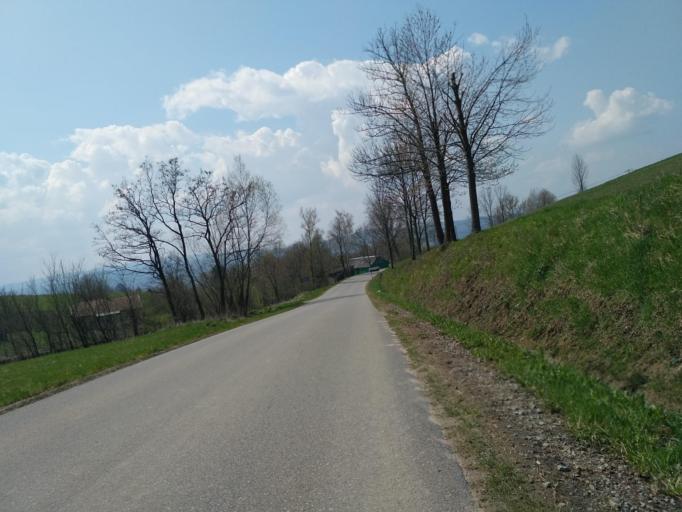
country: PL
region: Subcarpathian Voivodeship
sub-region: Powiat sanocki
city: Zarszyn
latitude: 49.5515
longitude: 21.9883
